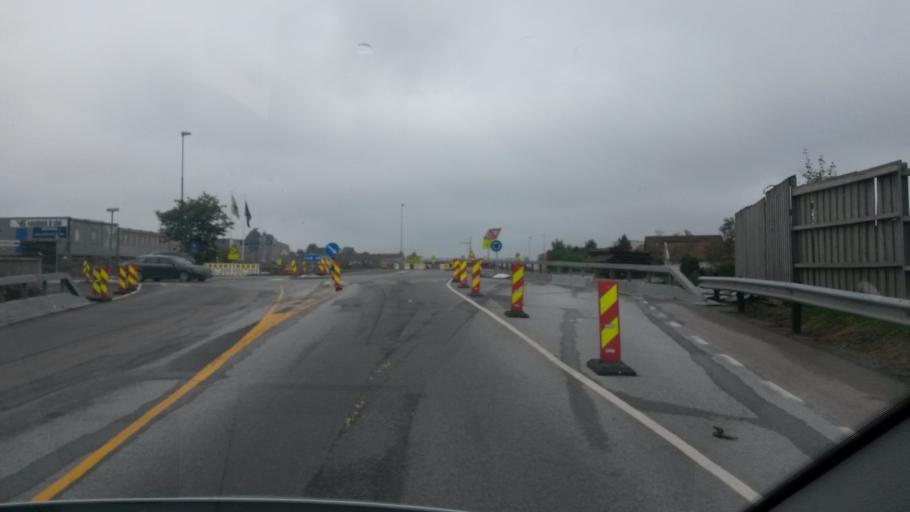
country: NO
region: Rogaland
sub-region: Sandnes
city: Sandnes
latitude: 58.8364
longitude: 5.7219
